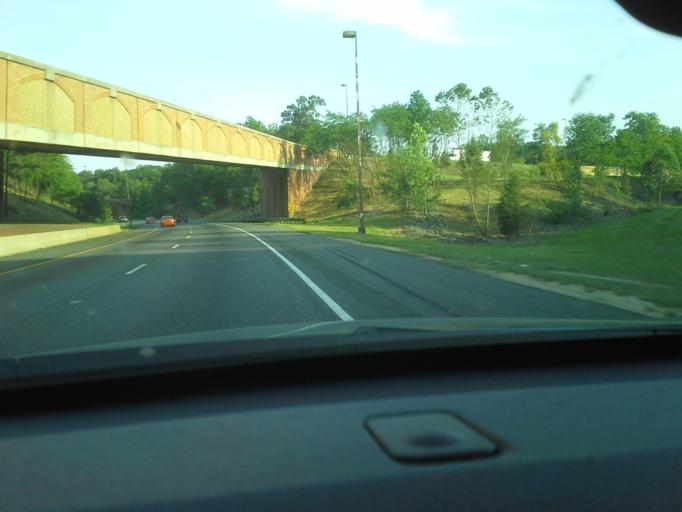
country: US
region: Maryland
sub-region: Anne Arundel County
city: Riva
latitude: 38.9870
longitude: -76.5778
